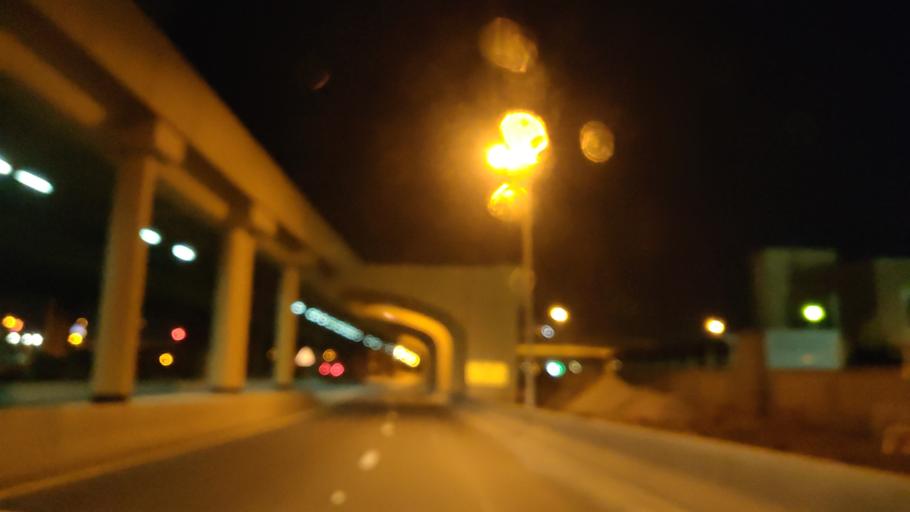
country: KW
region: Al Asimah
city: Ar Rabiyah
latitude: 29.3283
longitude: 47.9333
